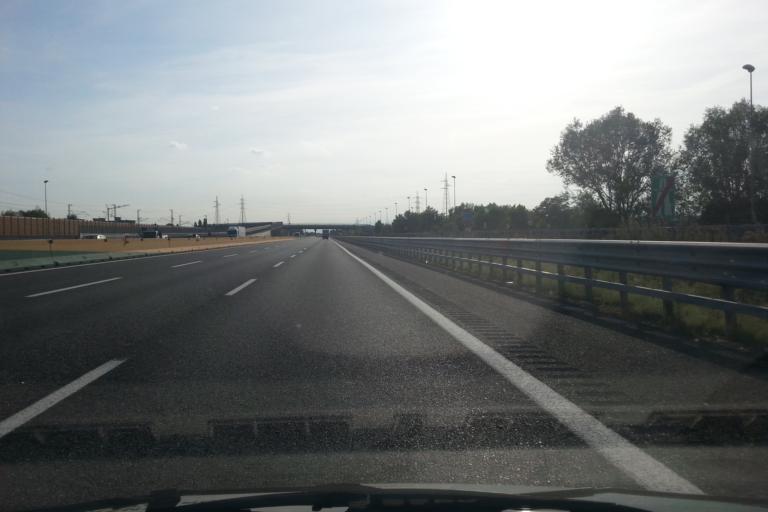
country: IT
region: Piedmont
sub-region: Provincia di Torino
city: Settimo Torinese
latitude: 45.1502
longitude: 7.7643
